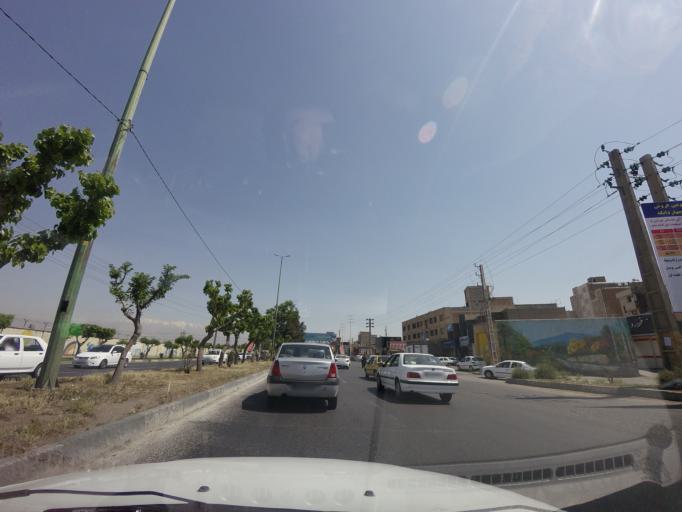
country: IR
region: Tehran
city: Eslamshahr
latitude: 35.6103
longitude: 51.3096
